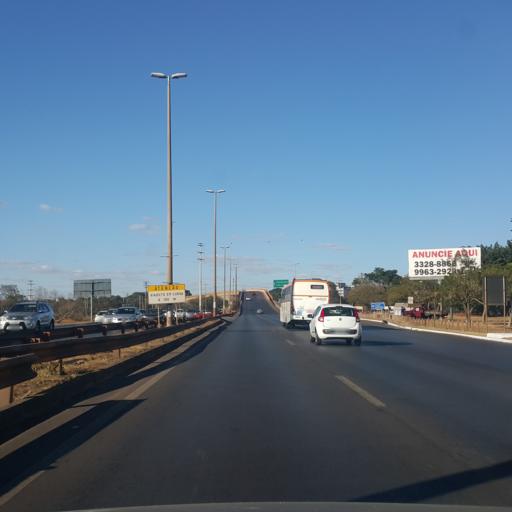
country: BR
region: Federal District
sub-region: Brasilia
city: Brasilia
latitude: -15.7869
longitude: -47.9450
